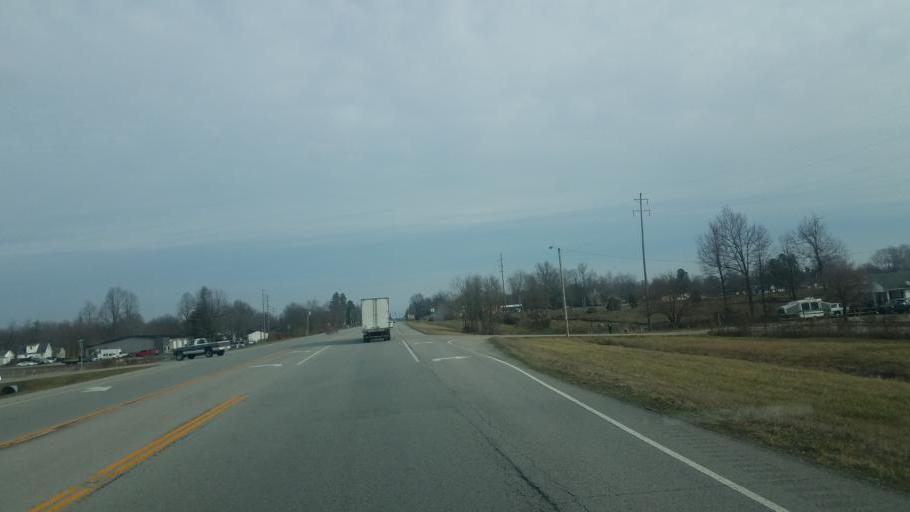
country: US
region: Kentucky
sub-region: Boyle County
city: Junction City
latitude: 37.5791
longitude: -84.7894
